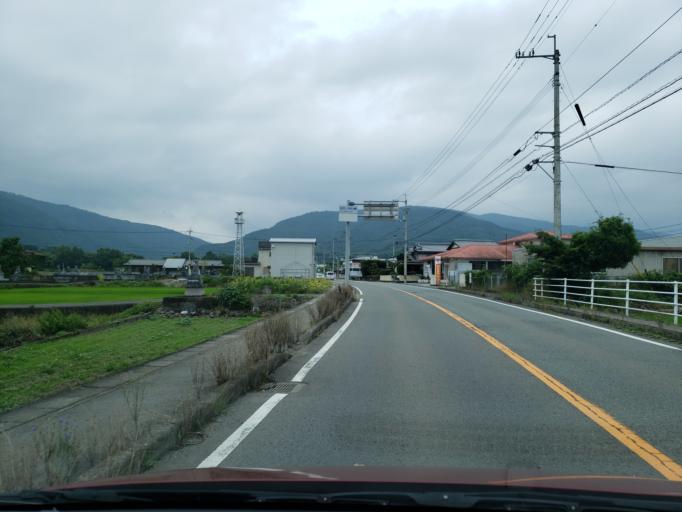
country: JP
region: Tokushima
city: Kamojimacho-jogejima
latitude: 34.1167
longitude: 134.3530
